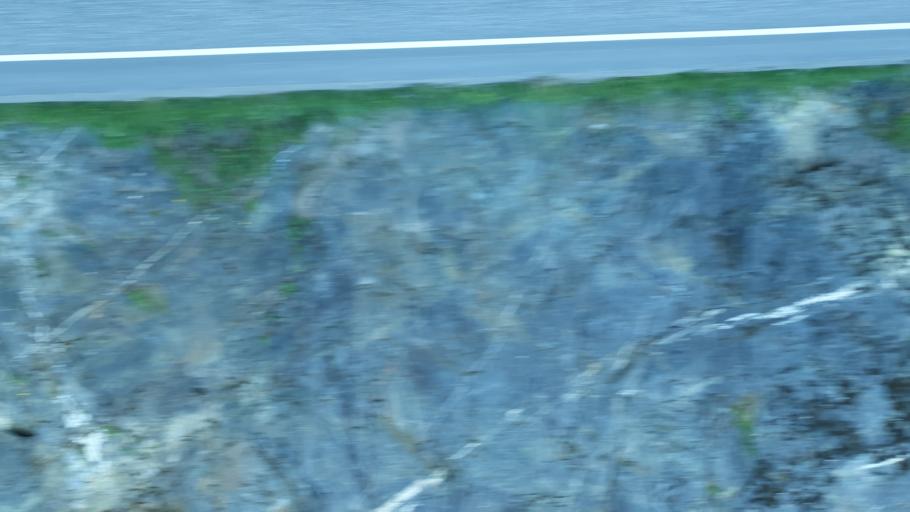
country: NO
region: Sor-Trondelag
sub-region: Rissa
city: Rissa
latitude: 63.5048
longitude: 10.1302
